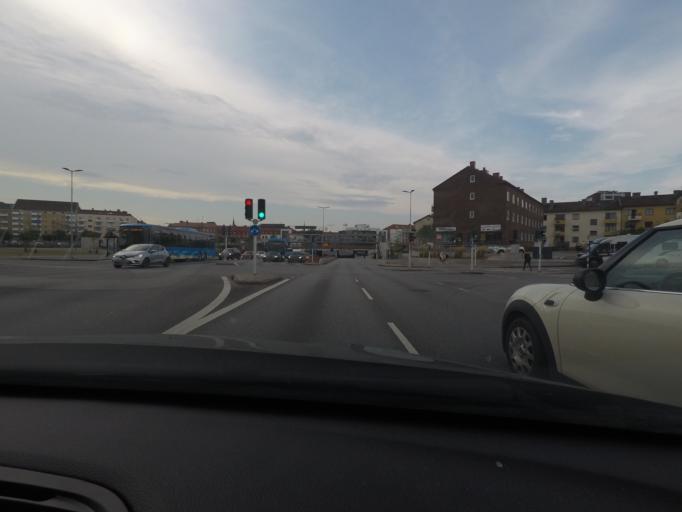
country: SE
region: Halland
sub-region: Halmstads Kommun
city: Halmstad
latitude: 56.6707
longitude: 12.8677
